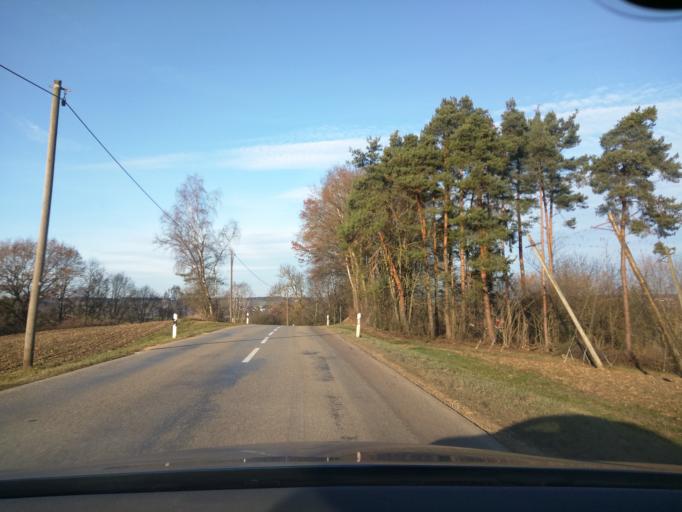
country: DE
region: Bavaria
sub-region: Upper Bavaria
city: Wolnzach
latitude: 48.5877
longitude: 11.6498
